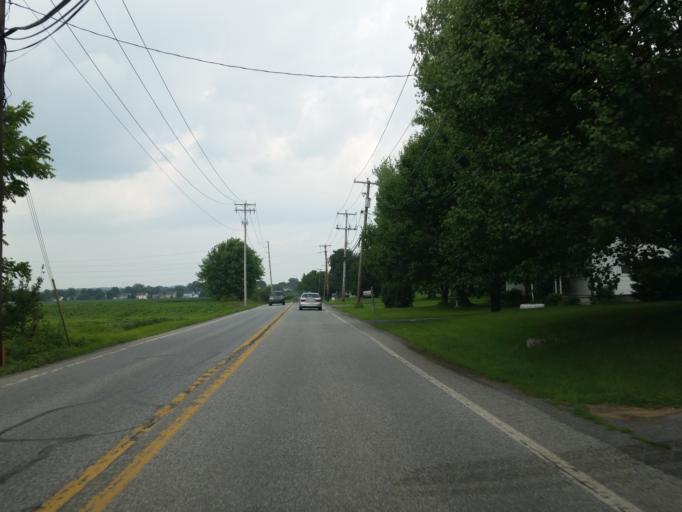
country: US
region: Pennsylvania
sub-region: Lebanon County
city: Campbelltown
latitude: 40.2896
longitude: -76.5748
